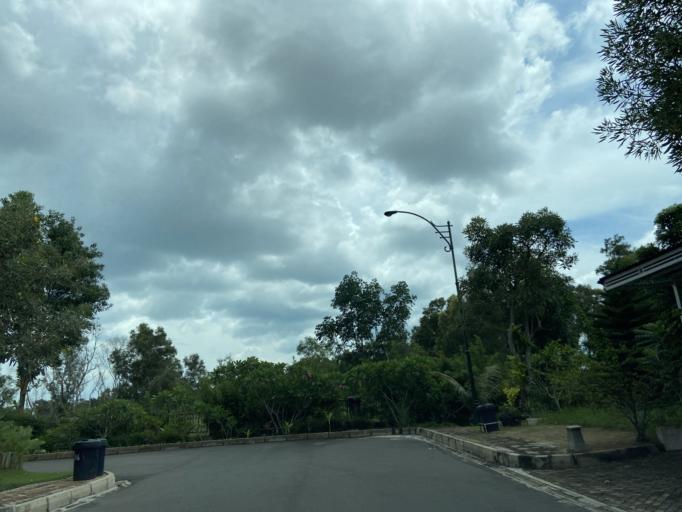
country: SG
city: Singapore
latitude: 1.1299
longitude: 103.9951
